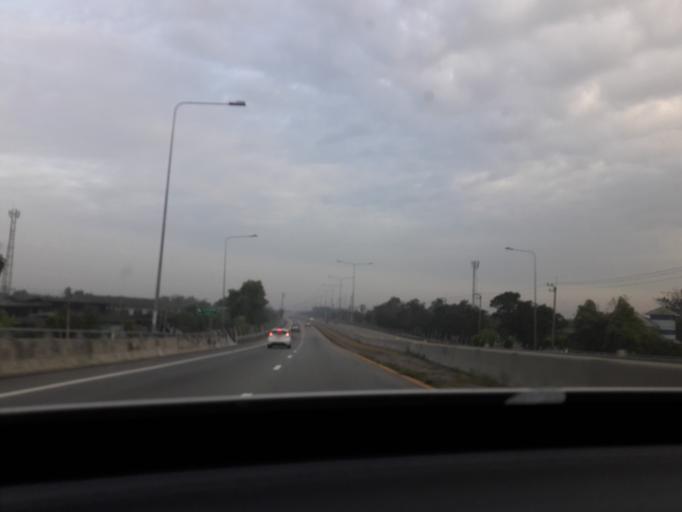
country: TH
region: Phra Nakhon Si Ayutthaya
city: Ban Bang Kadi Pathum Thani
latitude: 14.0434
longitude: 100.5810
